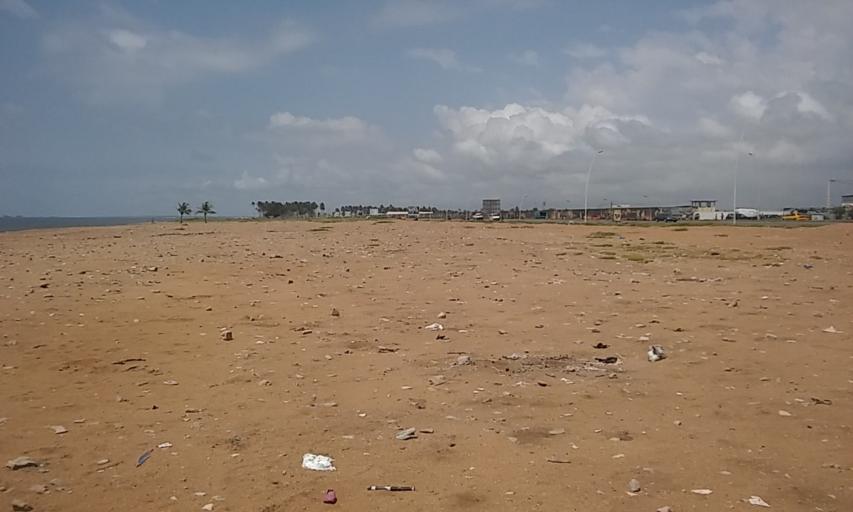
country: CI
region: Lagunes
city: Abidjan
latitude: 5.2439
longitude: -3.9291
